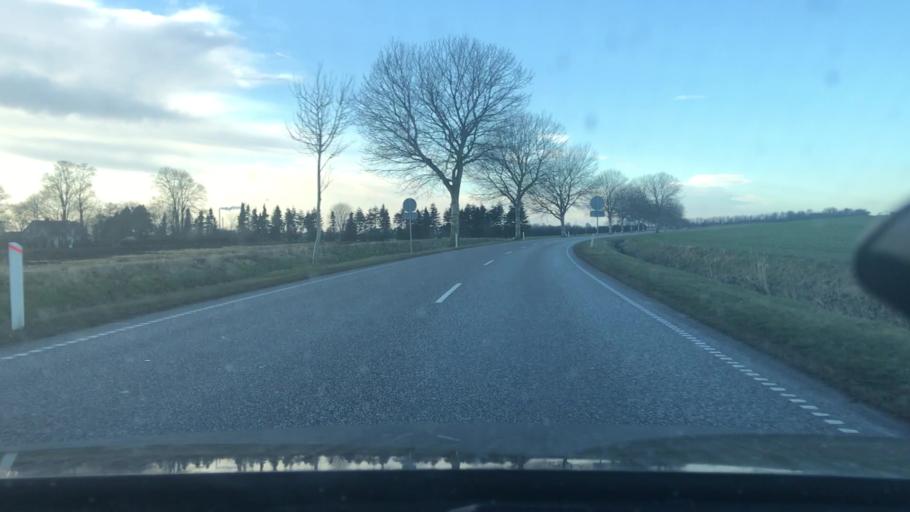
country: DK
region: Zealand
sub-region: Solrod Kommune
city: Solrod
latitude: 55.5160
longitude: 12.1733
